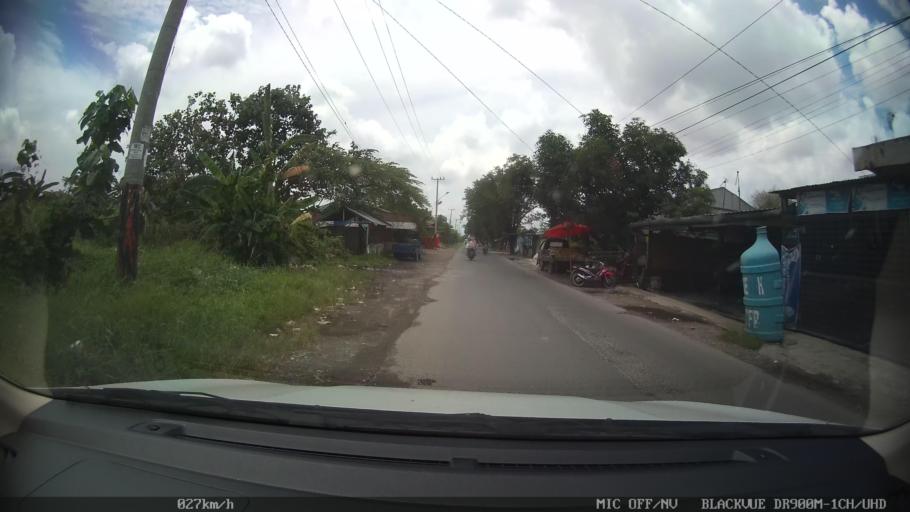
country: ID
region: North Sumatra
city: Medan
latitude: 3.6039
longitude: 98.7287
